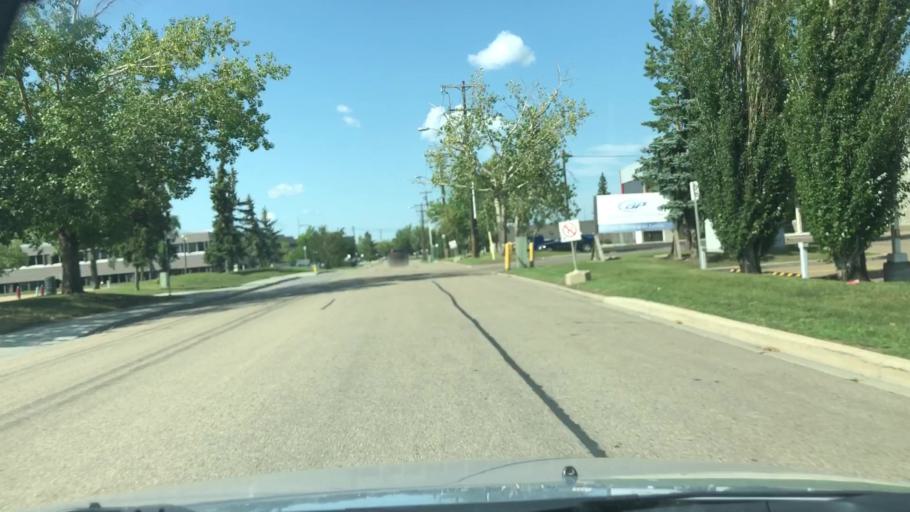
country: CA
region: Alberta
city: Edmonton
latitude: 53.5329
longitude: -113.4149
